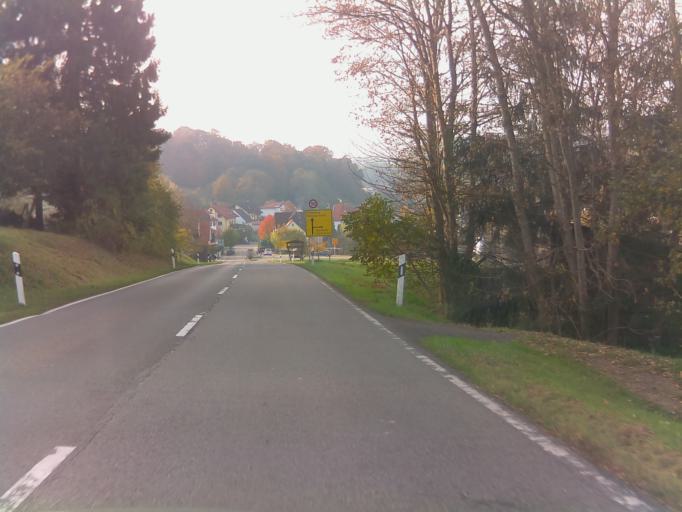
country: DE
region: Baden-Wuerttemberg
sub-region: Karlsruhe Region
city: Spechbach
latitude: 49.3721
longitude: 8.9021
